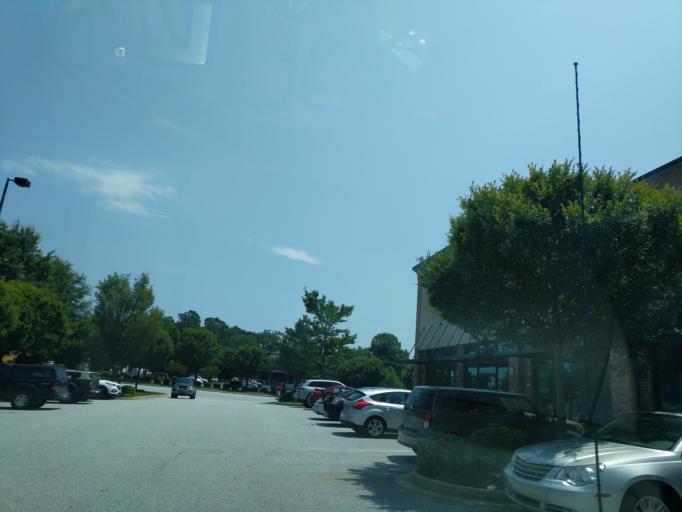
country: US
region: South Carolina
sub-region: Greenville County
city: Mauldin
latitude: 34.8255
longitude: -82.3002
